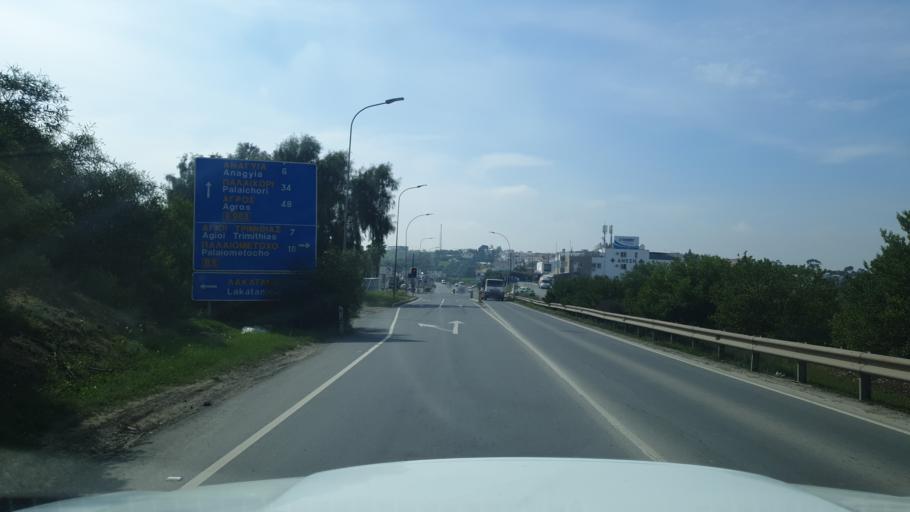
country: CY
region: Lefkosia
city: Kato Deftera
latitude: 35.1167
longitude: 33.2866
